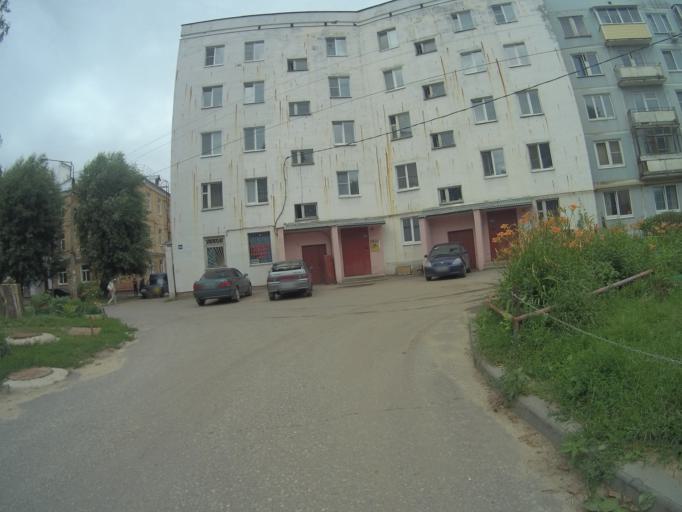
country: RU
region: Vladimir
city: Vladimir
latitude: 56.1284
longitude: 40.3716
